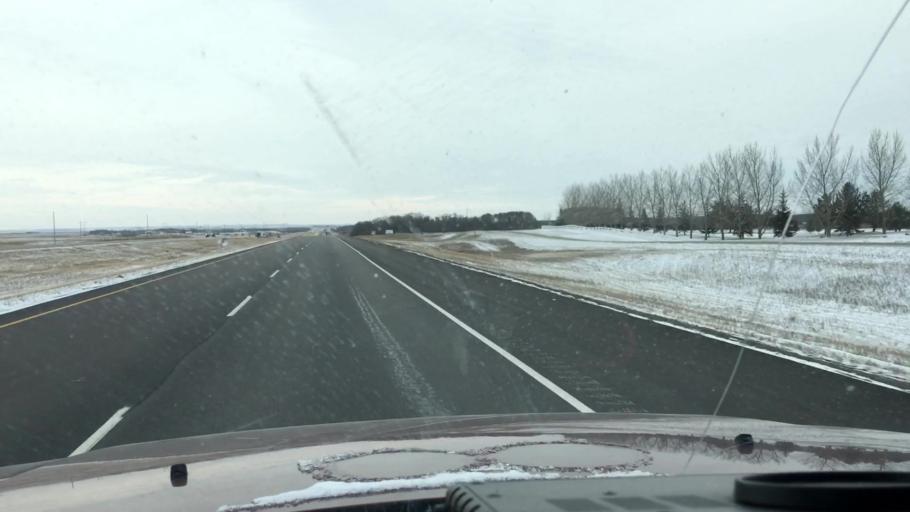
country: CA
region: Saskatchewan
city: Saskatoon
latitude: 51.9060
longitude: -106.5242
